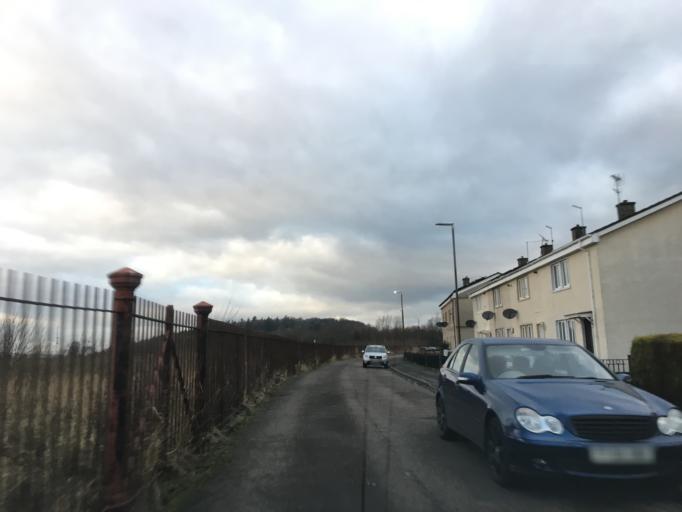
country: GB
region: Scotland
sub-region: Stirling
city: Stirling
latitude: 56.1260
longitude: -3.9559
